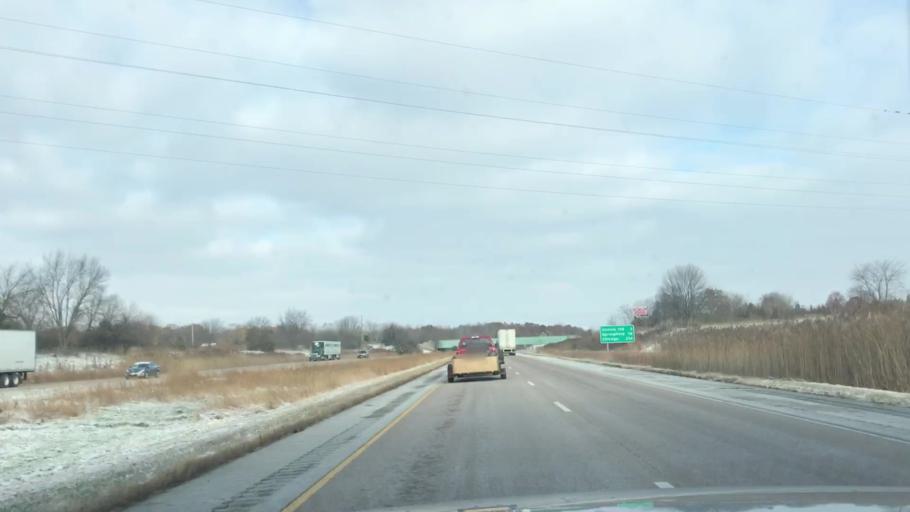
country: US
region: Illinois
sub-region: Macoupin County
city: Staunton
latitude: 39.0322
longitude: -89.7533
